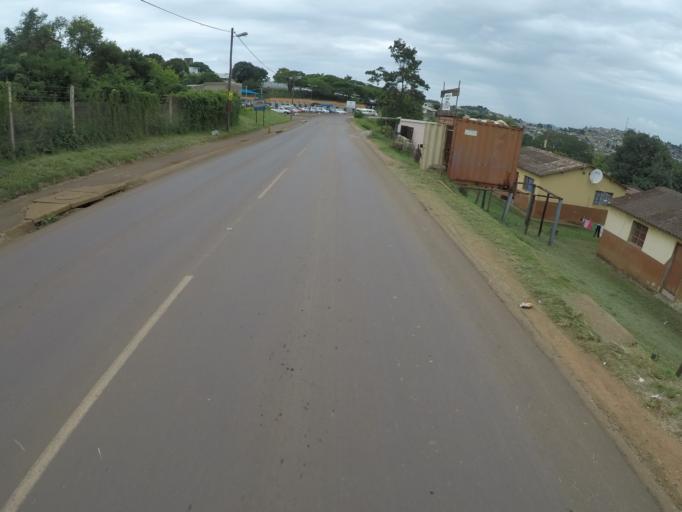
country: ZA
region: KwaZulu-Natal
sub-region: uThungulu District Municipality
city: Empangeni
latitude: -28.7759
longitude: 31.8650
